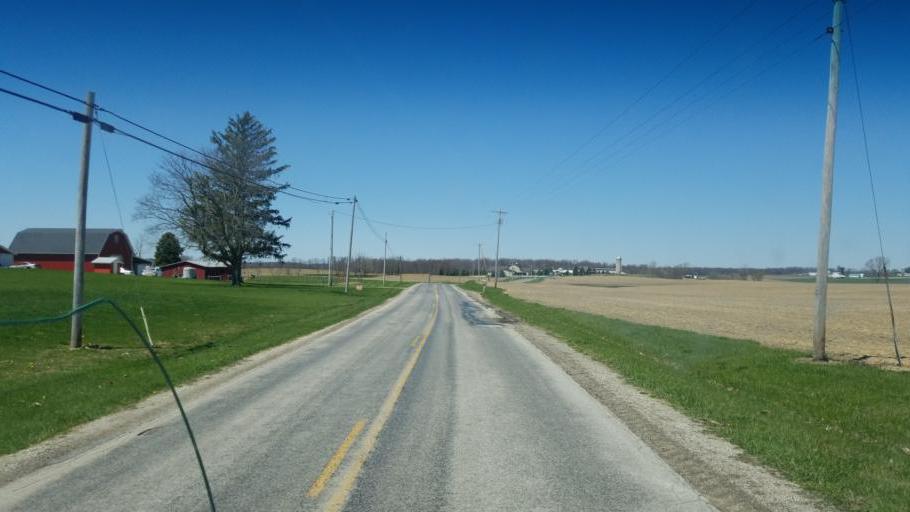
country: US
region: Ohio
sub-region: Richland County
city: Shelby
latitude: 40.9200
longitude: -82.5753
